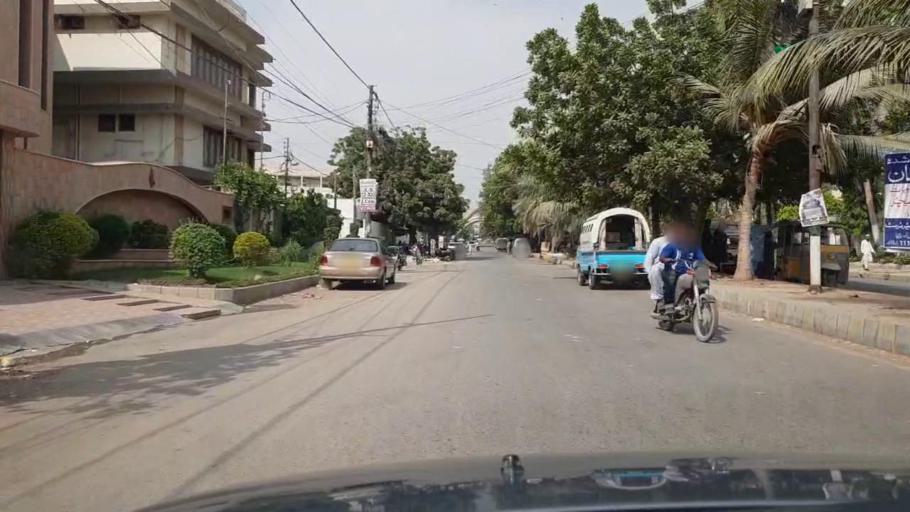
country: PK
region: Sindh
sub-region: Karachi District
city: Karachi
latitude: 24.8748
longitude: 67.0860
